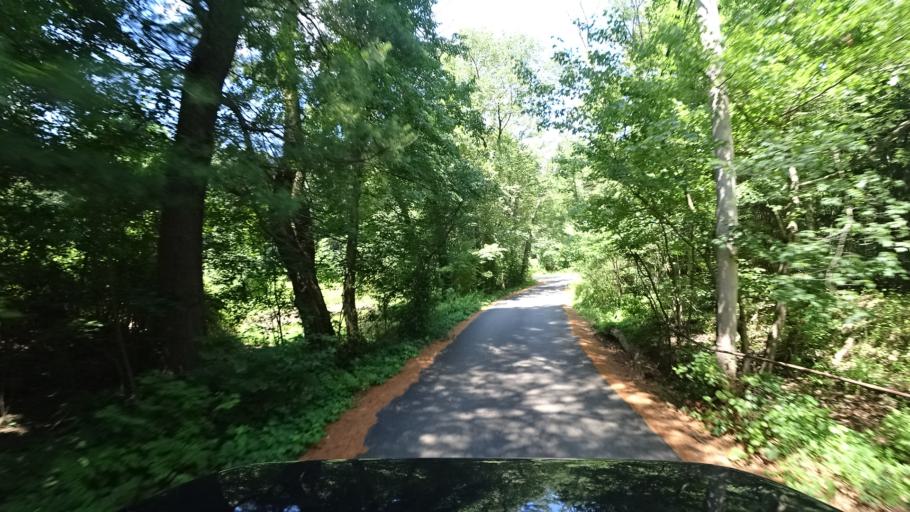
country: US
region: Massachusetts
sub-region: Norfolk County
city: Dedham
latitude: 42.2531
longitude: -71.1964
